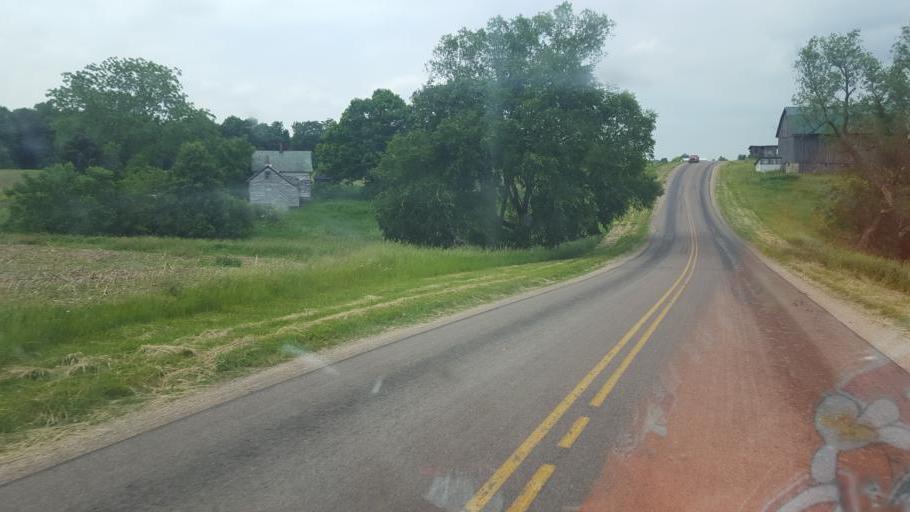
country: US
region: Wisconsin
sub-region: Vernon County
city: Hillsboro
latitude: 43.5975
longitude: -90.4151
